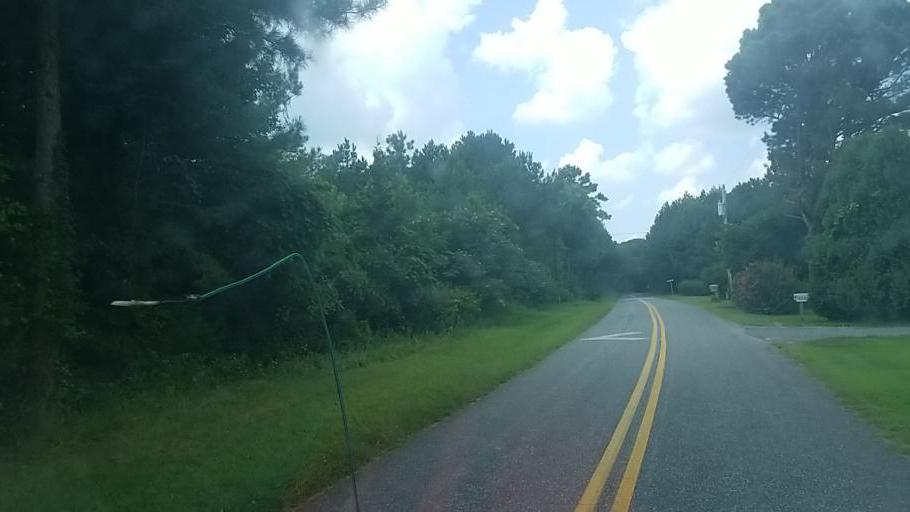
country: US
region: Maryland
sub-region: Worcester County
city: Snow Hill
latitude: 38.2612
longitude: -75.4529
